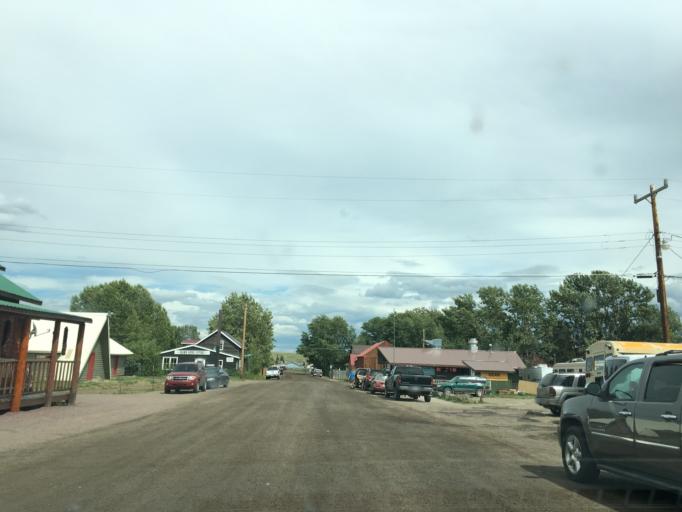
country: US
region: Montana
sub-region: Glacier County
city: South Browning
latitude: 48.4420
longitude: -113.2181
